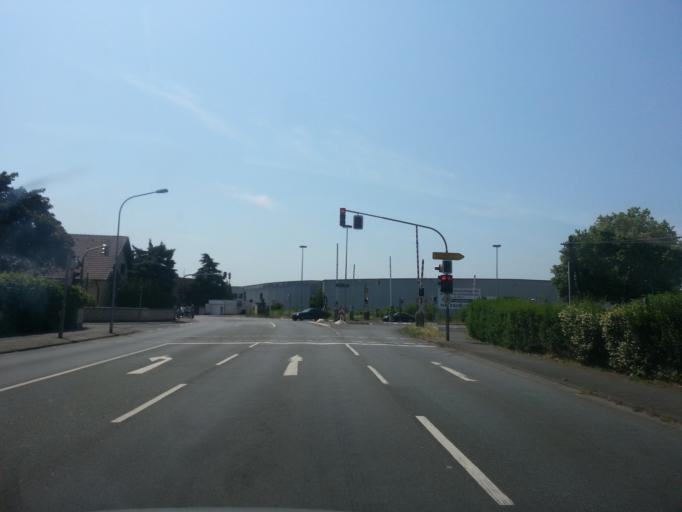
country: DE
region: Hesse
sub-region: Regierungsbezirk Darmstadt
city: Eppertshausen
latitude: 49.9499
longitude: 8.8402
